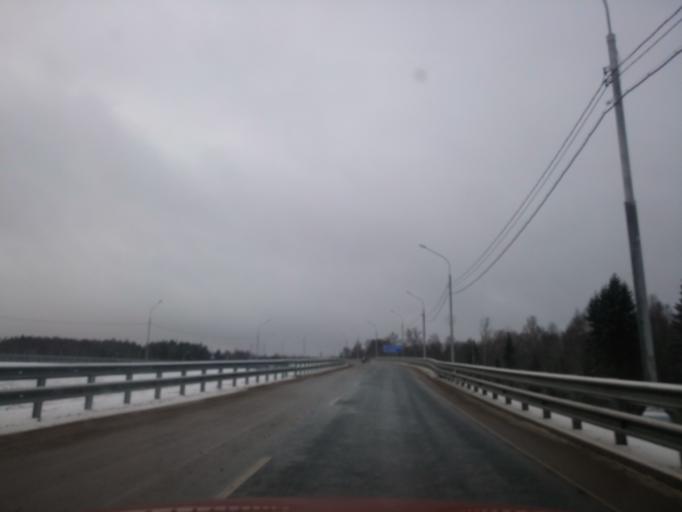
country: RU
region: Tverskaya
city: Likhoslavl'
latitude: 56.9478
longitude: 35.5014
